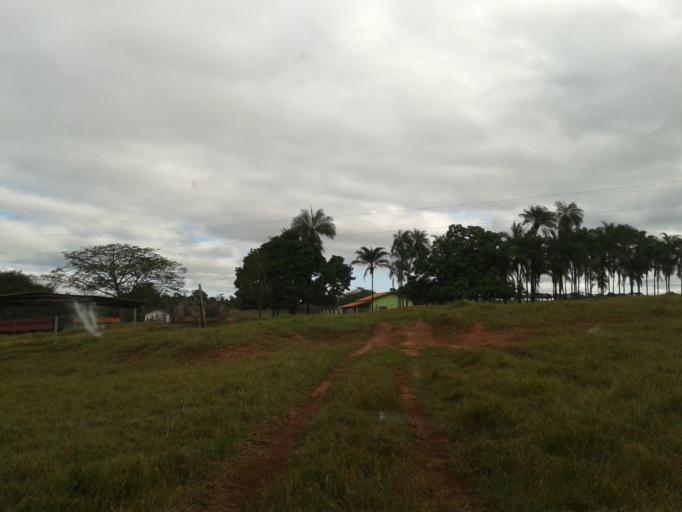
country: BR
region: Minas Gerais
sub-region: Campina Verde
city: Campina Verde
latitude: -19.4860
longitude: -49.6506
